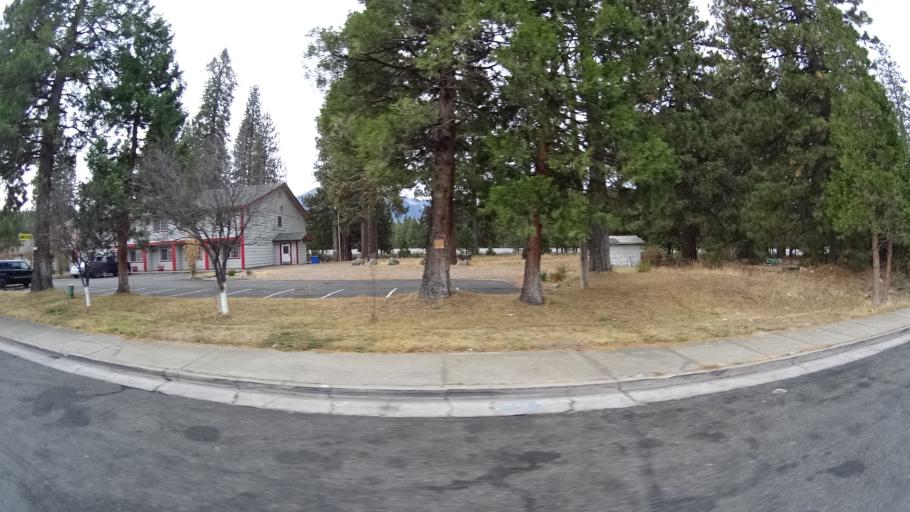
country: US
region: California
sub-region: Siskiyou County
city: Weed
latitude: 41.3996
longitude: -122.3808
